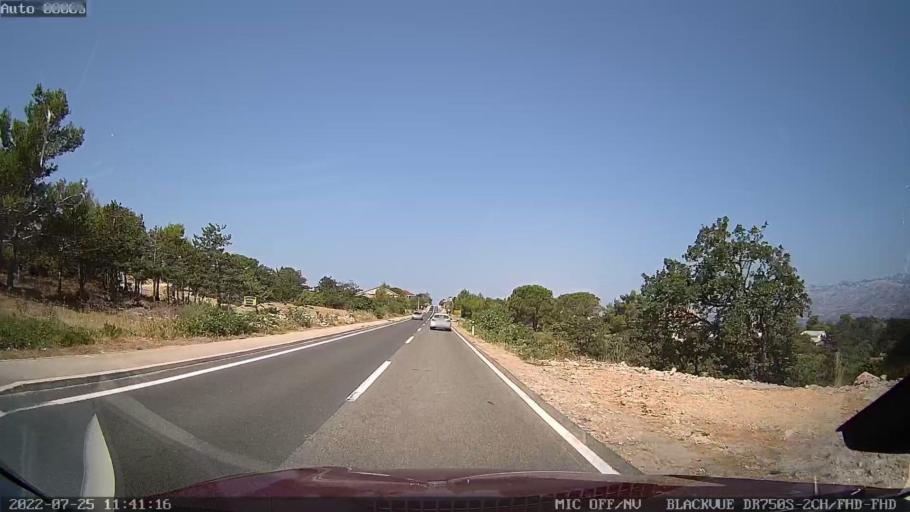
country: HR
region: Zadarska
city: Razanac
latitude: 44.2676
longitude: 15.3493
